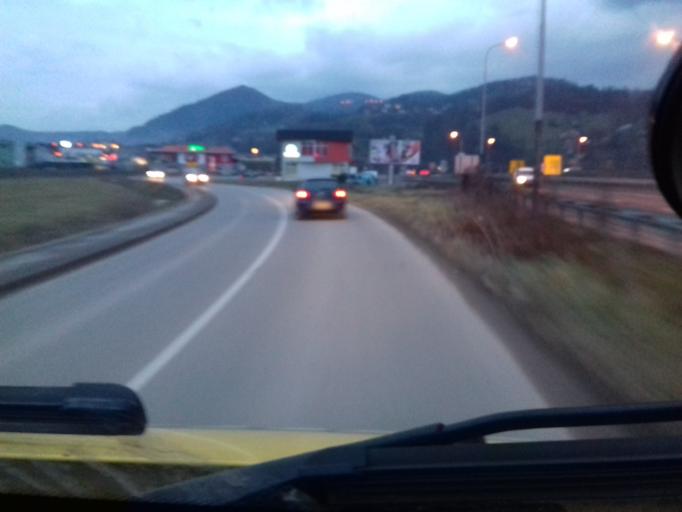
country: BA
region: Federation of Bosnia and Herzegovina
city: Visoko
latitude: 44.0013
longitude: 18.1665
